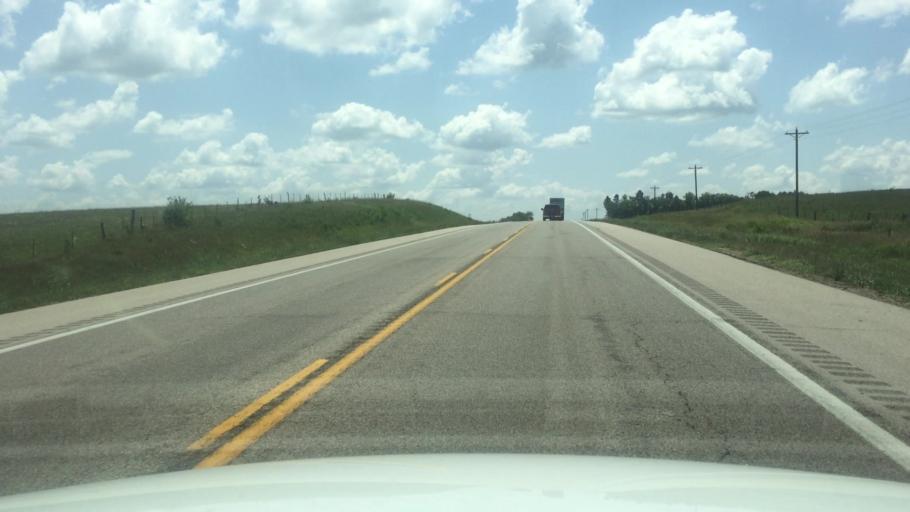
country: US
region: Kansas
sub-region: Brown County
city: Horton
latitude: 39.6789
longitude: -95.7306
